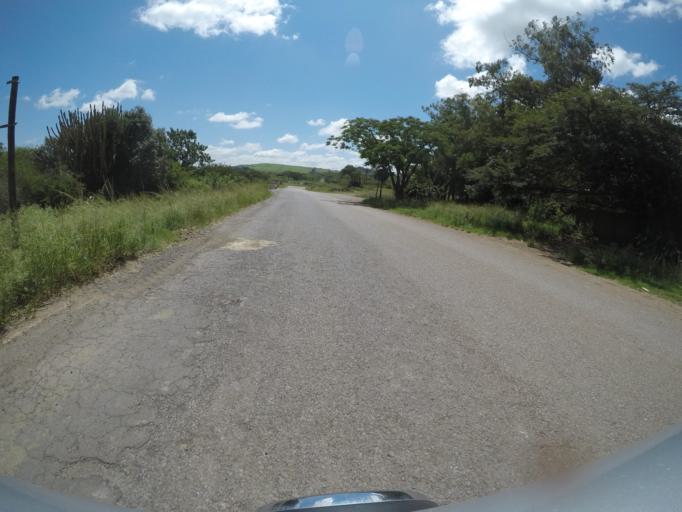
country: ZA
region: KwaZulu-Natal
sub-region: uThungulu District Municipality
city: Empangeni
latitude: -28.6629
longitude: 31.7856
